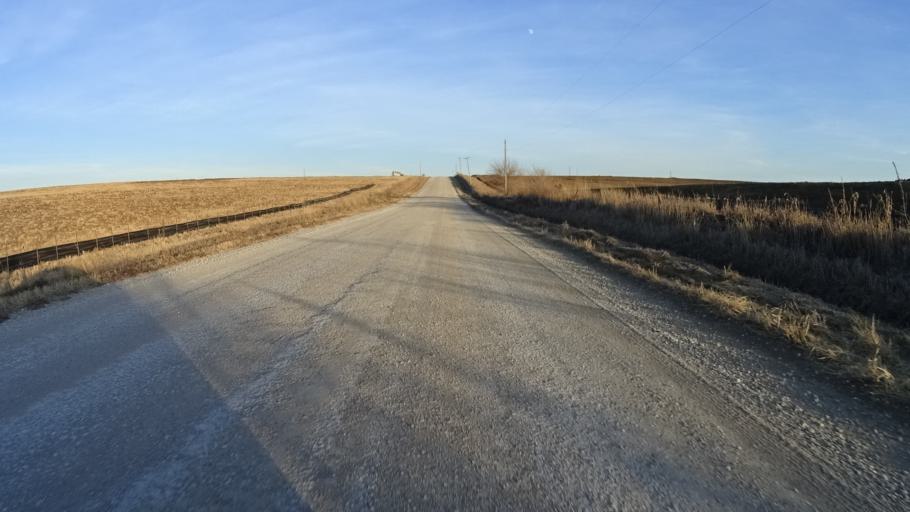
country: US
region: Nebraska
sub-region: Sarpy County
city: Papillion
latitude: 41.1326
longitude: -96.0984
